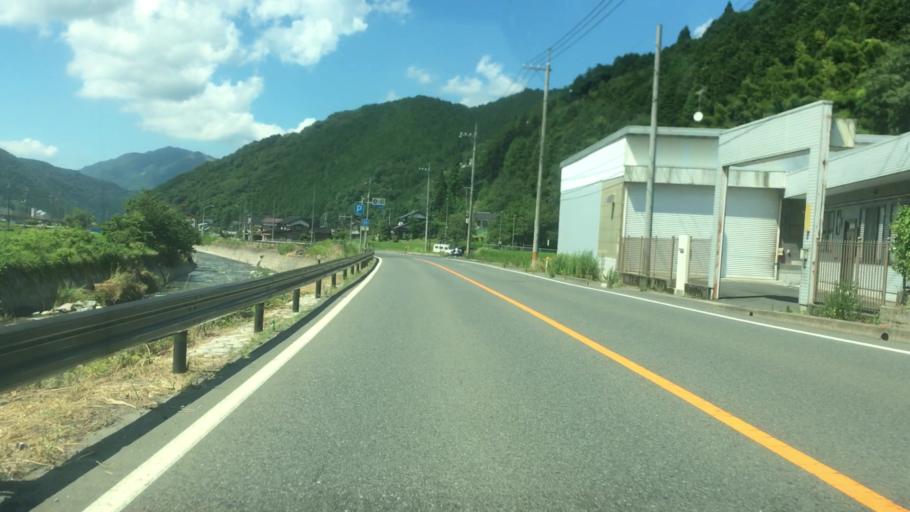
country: JP
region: Tottori
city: Tottori
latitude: 35.2485
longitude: 134.2304
